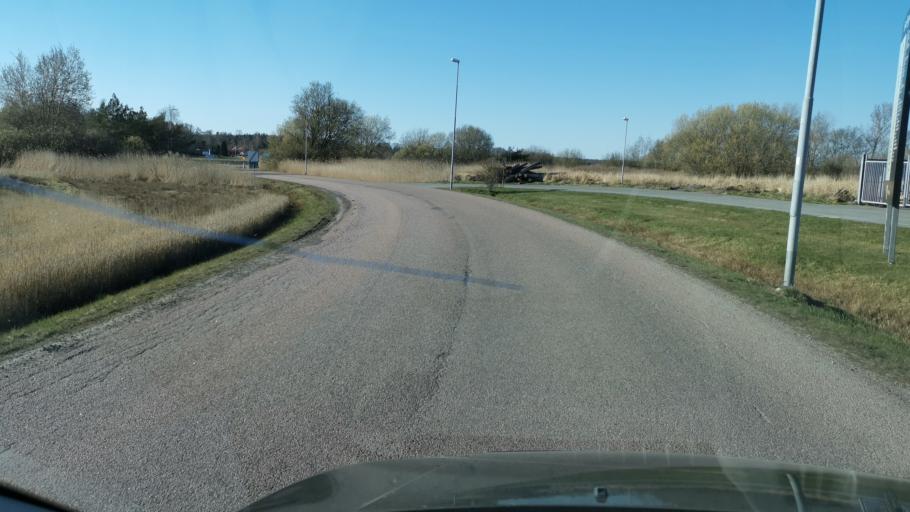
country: SE
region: Vaestra Goetaland
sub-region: Goteborg
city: Majorna
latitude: 57.7838
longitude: 11.8603
